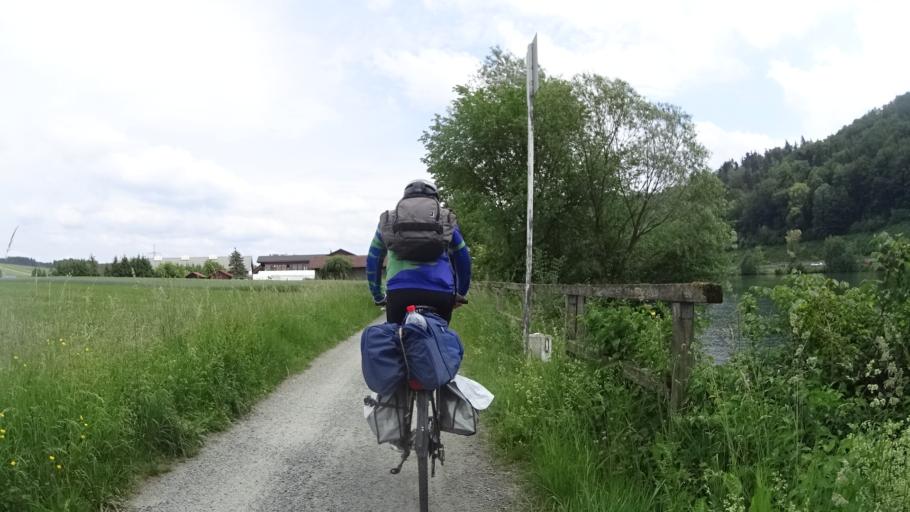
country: DE
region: Bavaria
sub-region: Lower Bavaria
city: Tiefenbach
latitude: 48.6043
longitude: 13.3207
